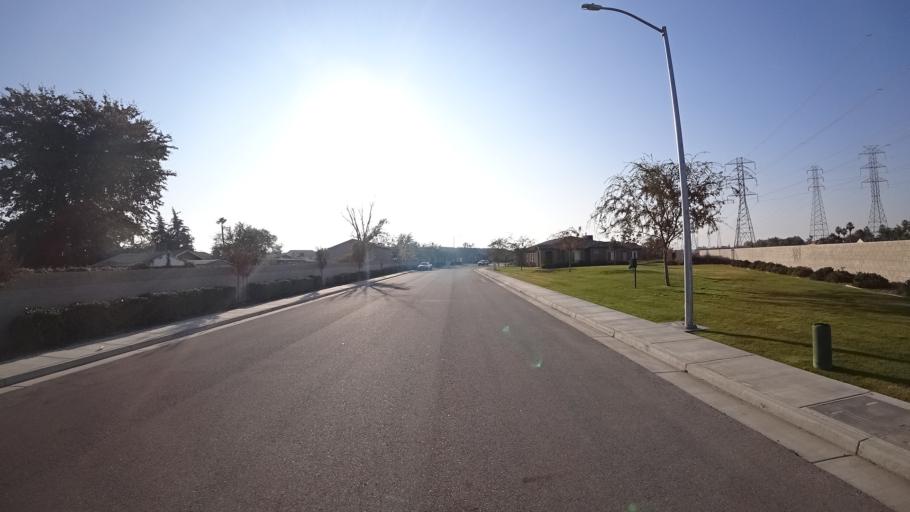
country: US
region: California
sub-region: Kern County
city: Rosedale
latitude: 35.3863
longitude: -119.1468
